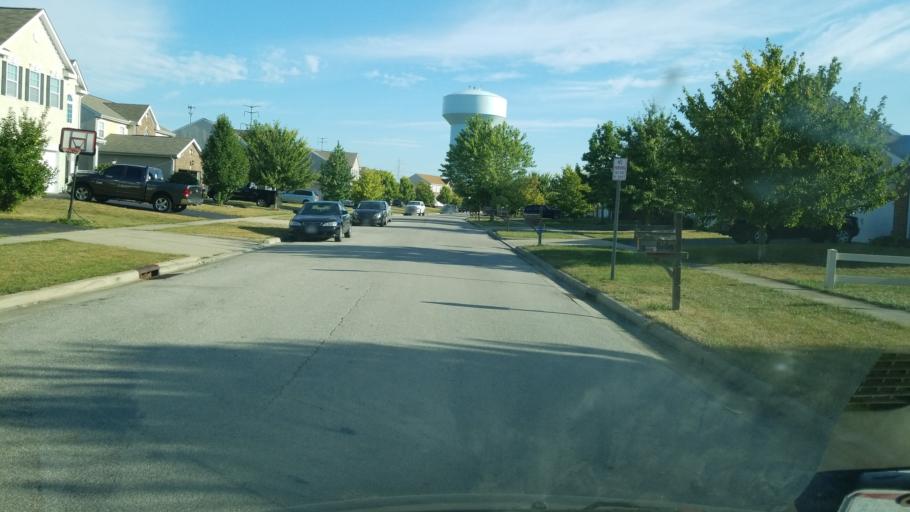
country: US
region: Ohio
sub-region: Delaware County
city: Lewis Center
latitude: 40.1716
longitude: -83.0066
